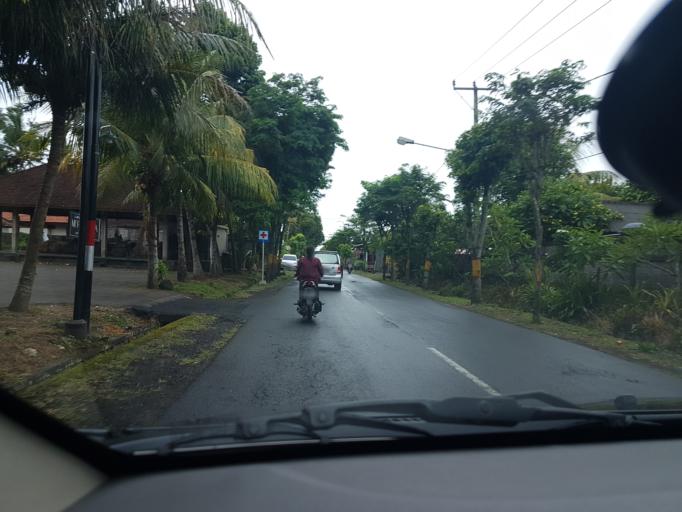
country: ID
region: Bali
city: Banjar Sedang
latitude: -8.5754
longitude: 115.2383
